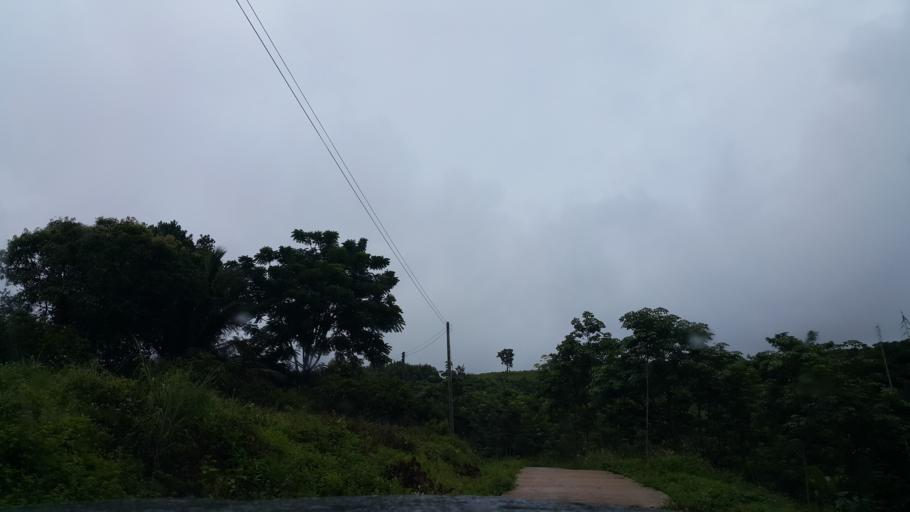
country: TH
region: Phayao
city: Chiang Kham
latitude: 19.4959
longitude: 100.4635
